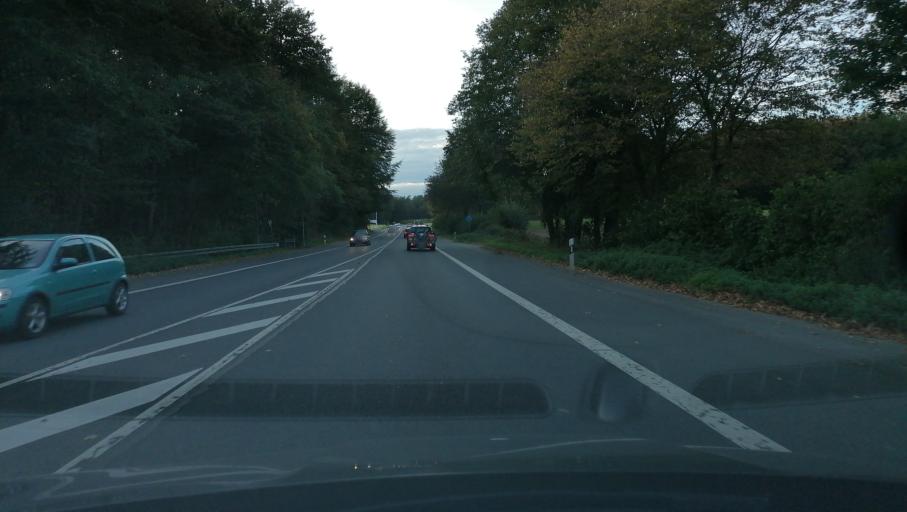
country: DE
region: North Rhine-Westphalia
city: Herten
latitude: 51.6347
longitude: 7.1348
